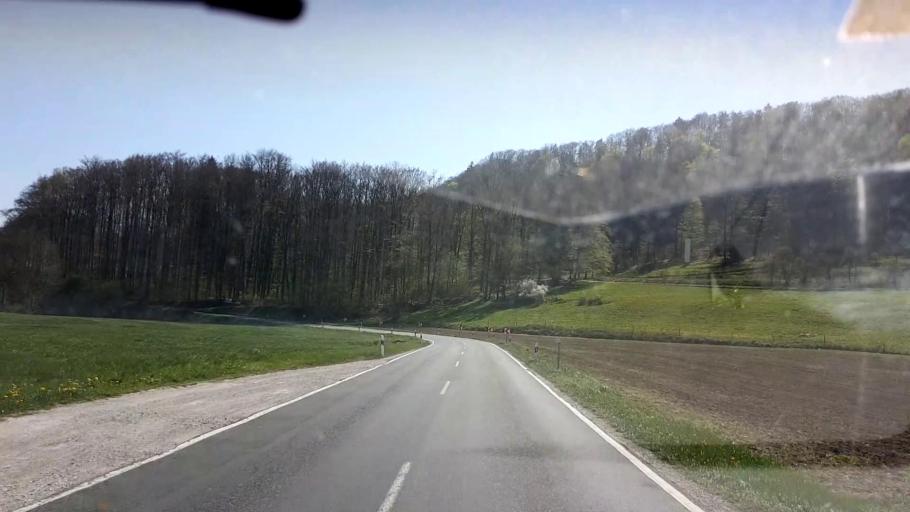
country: DE
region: Bavaria
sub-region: Upper Franconia
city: Unterleinleiter
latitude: 49.8296
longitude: 11.1875
